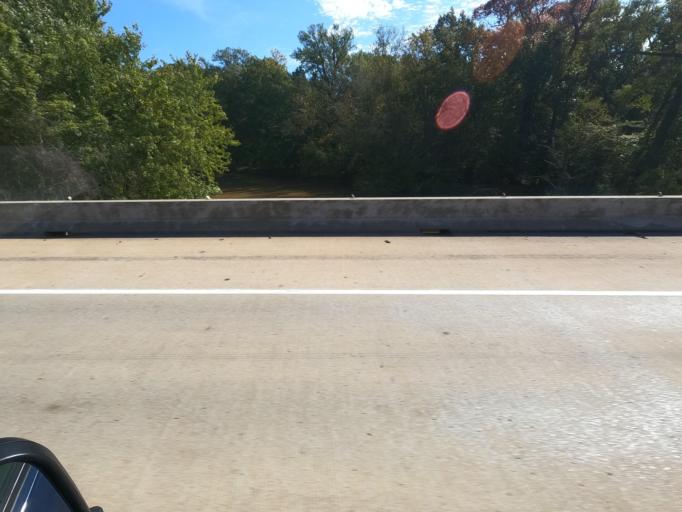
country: US
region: Tennessee
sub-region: Haywood County
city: Brownsville
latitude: 35.5249
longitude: -89.2592
